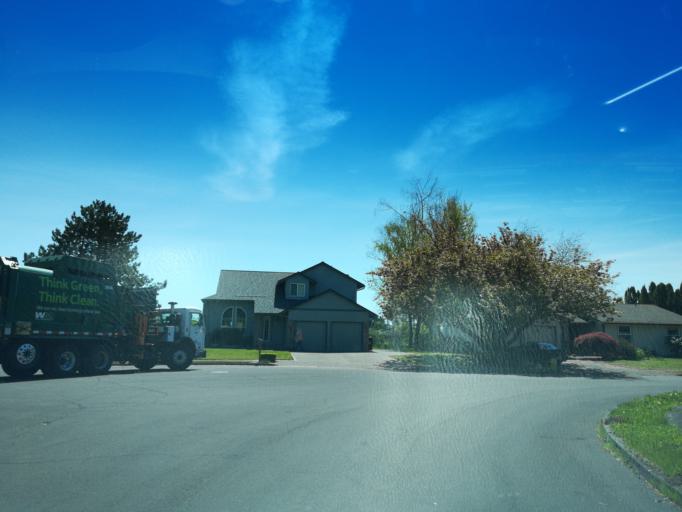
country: US
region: Oregon
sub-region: Multnomah County
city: Troutdale
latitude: 45.5277
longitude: -122.3913
